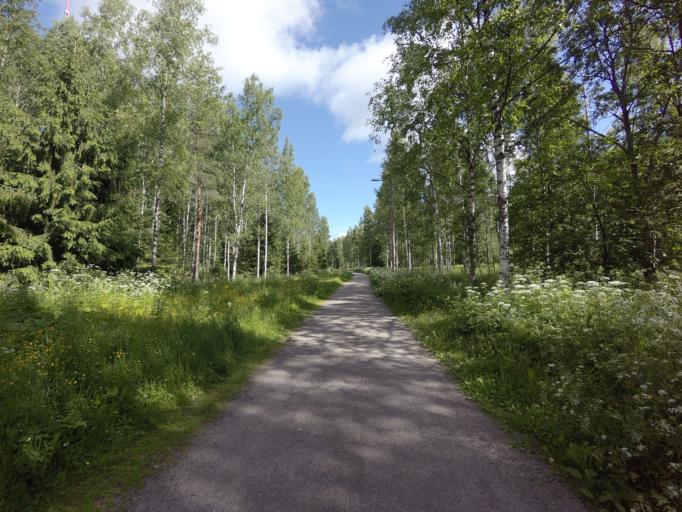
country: FI
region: Uusimaa
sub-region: Helsinki
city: Espoo
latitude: 60.1752
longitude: 24.6462
